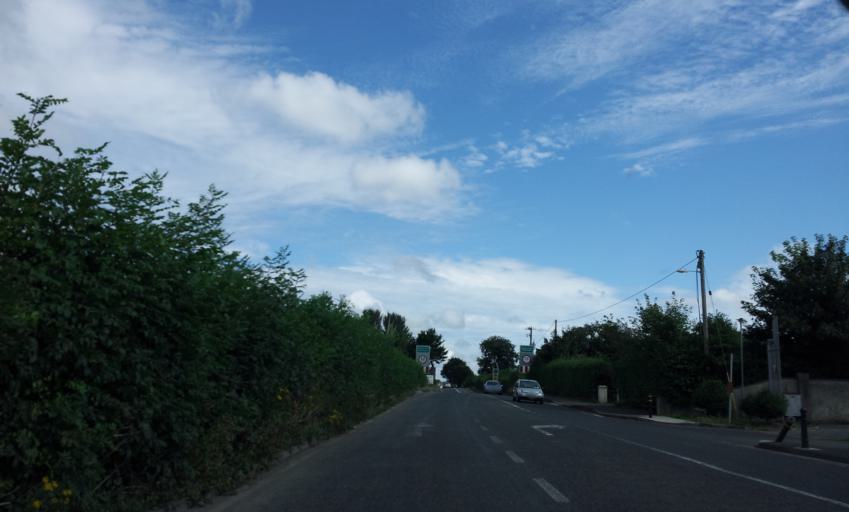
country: IE
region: Leinster
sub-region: Laois
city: Mountrath
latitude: 52.9927
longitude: -7.4842
